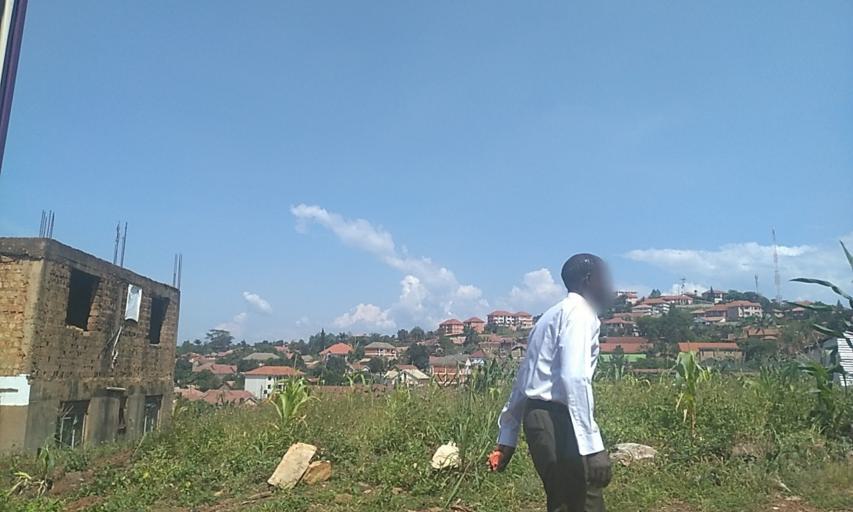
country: UG
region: Central Region
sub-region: Wakiso District
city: Kireka
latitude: 0.3720
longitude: 32.6017
